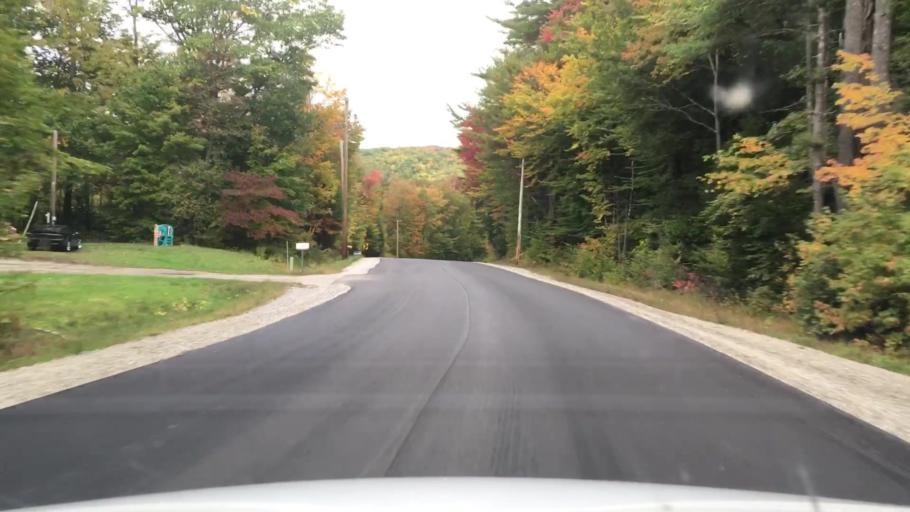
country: US
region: Maine
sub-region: Oxford County
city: Bethel
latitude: 44.3203
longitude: -70.7647
